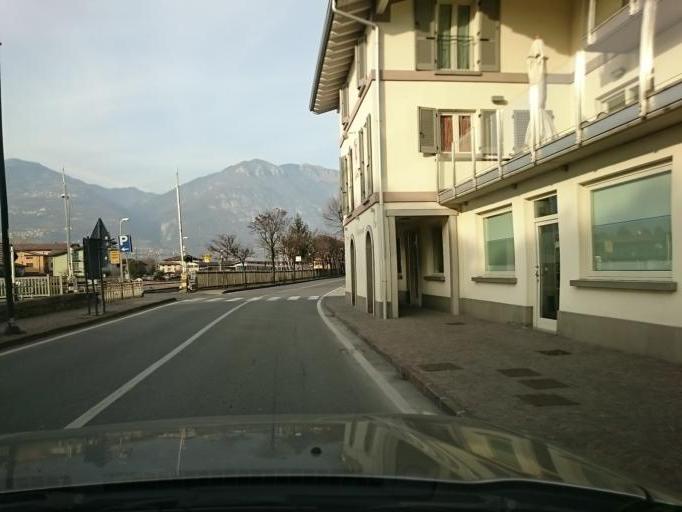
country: IT
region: Lombardy
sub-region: Provincia di Brescia
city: Pisogne
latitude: 45.8052
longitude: 10.1060
